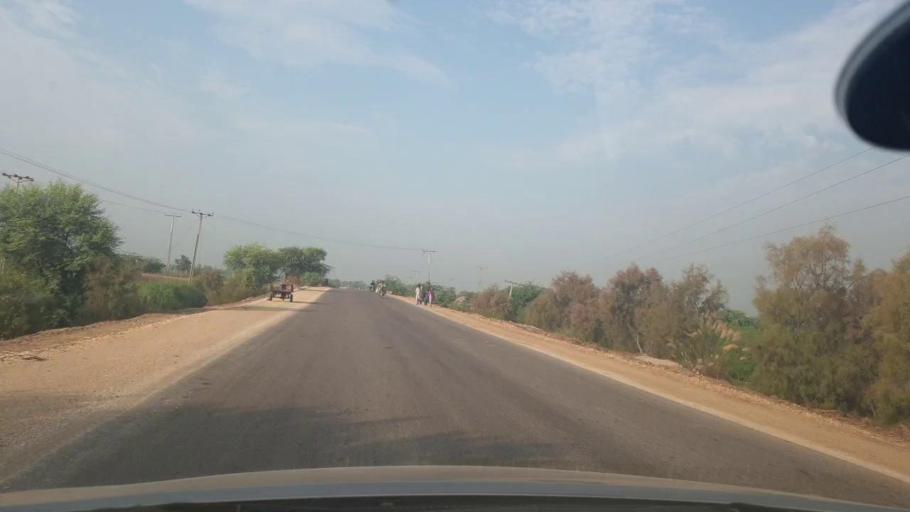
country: PK
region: Sindh
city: Jacobabad
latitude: 28.2516
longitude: 68.4054
